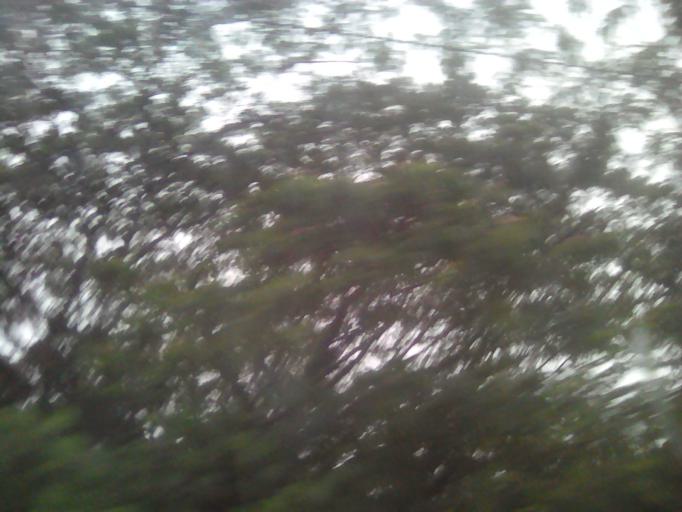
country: MY
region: Kedah
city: Kulim
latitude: 5.3884
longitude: 100.5466
